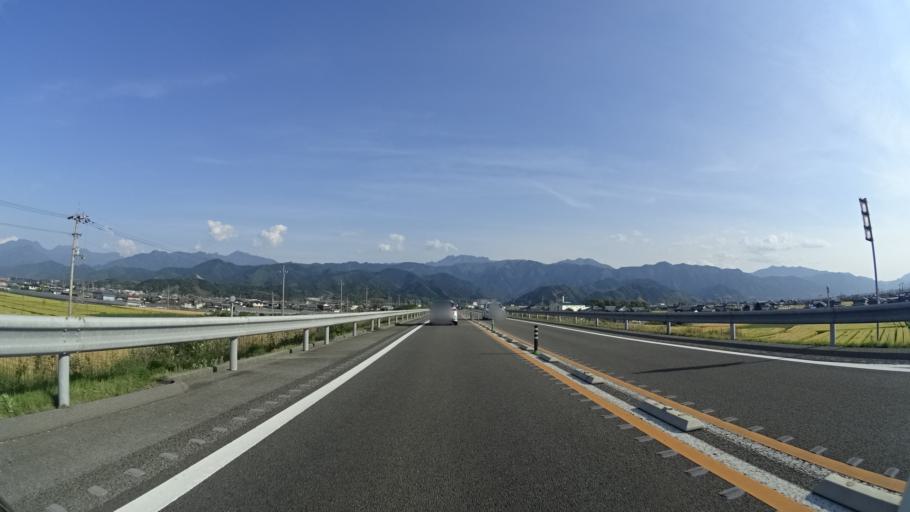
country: JP
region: Ehime
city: Saijo
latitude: 33.9039
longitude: 133.0754
